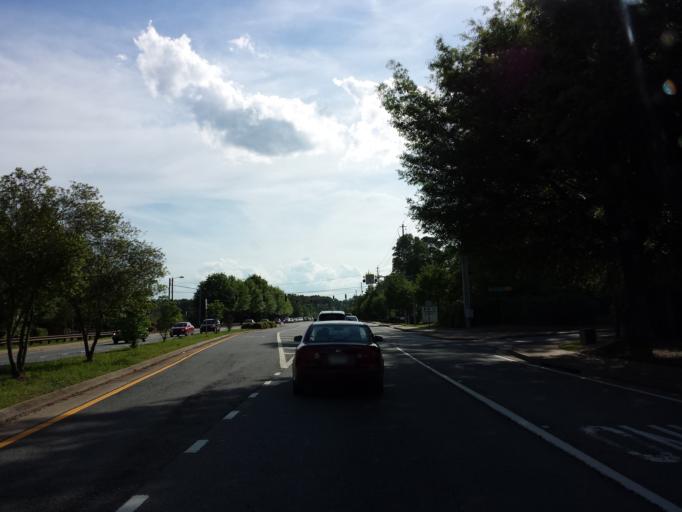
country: US
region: Georgia
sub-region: Cobb County
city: Marietta
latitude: 33.9507
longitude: -84.5838
